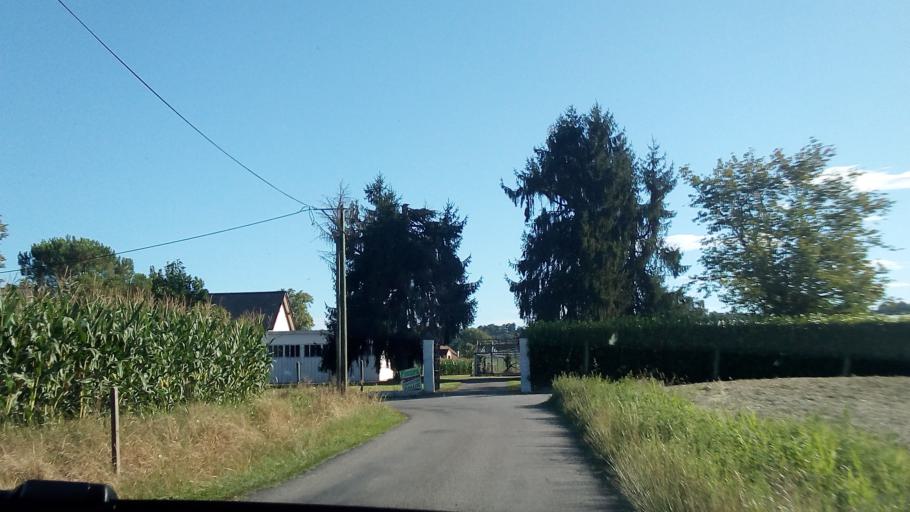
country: FR
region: Aquitaine
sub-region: Departement des Pyrenees-Atlantiques
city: Nousty
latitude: 43.2717
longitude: -0.2063
